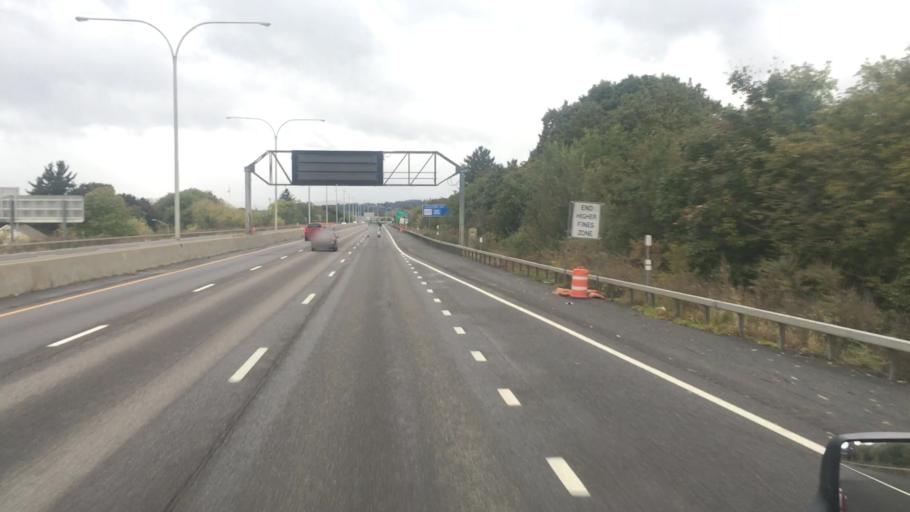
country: US
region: New York
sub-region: Broome County
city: Johnson City
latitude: 42.1198
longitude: -75.9515
